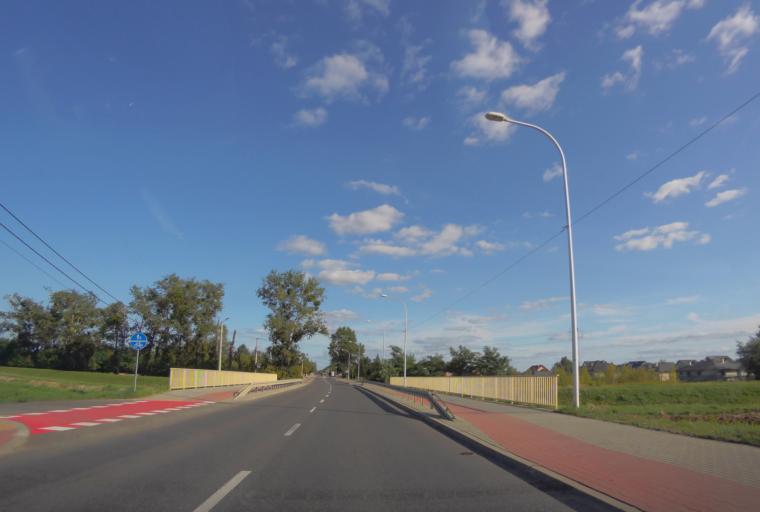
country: PL
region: Subcarpathian Voivodeship
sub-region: Tarnobrzeg
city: Tarnobrzeg
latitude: 50.5668
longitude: 21.7235
